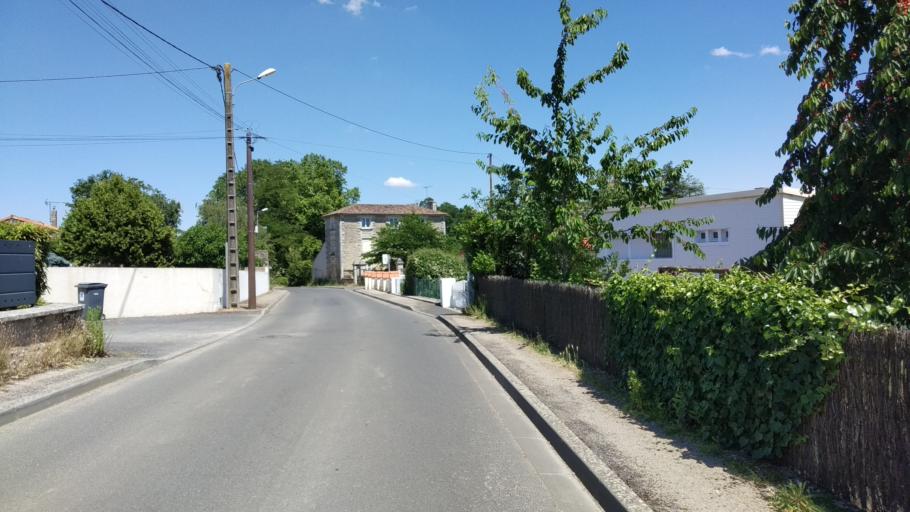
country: FR
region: Poitou-Charentes
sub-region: Departement de la Vienne
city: Vouneuil-sous-Biard
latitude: 46.6081
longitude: 0.2751
